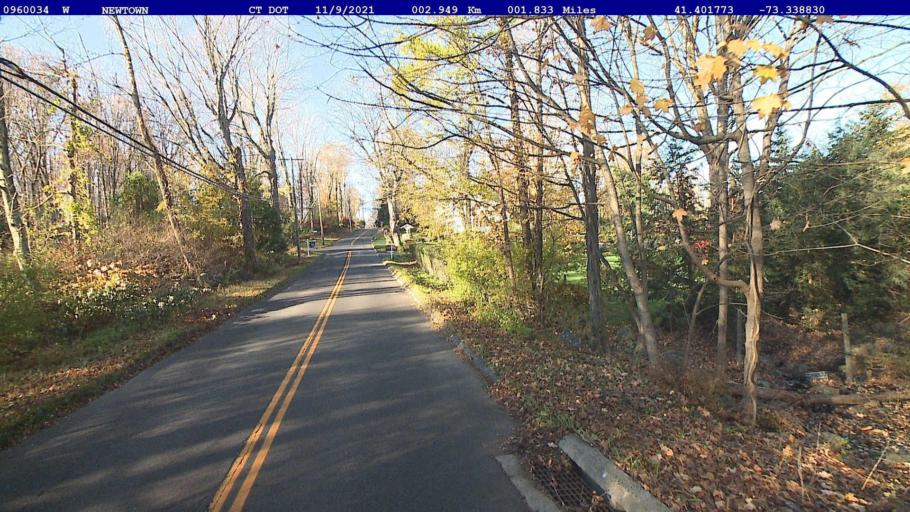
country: US
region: Connecticut
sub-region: Fairfield County
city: Newtown
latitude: 41.4018
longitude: -73.3388
